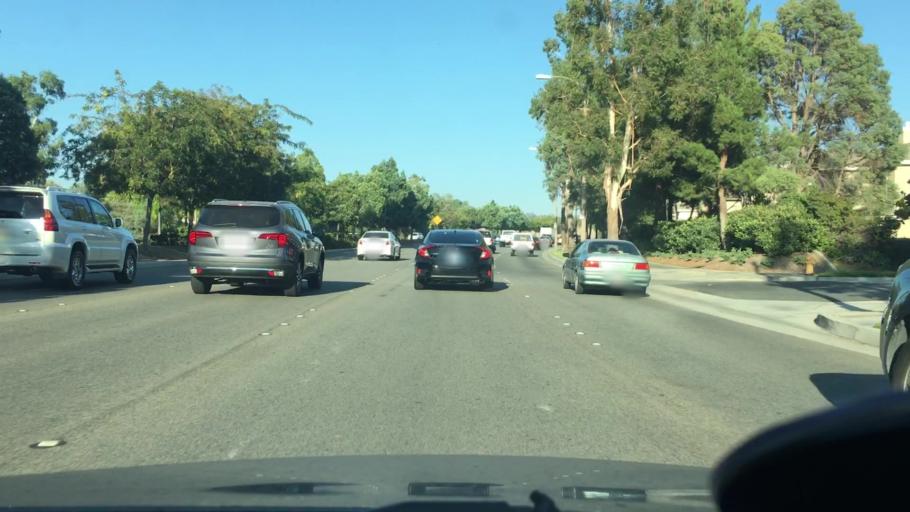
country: US
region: California
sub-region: Los Angeles County
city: Santa Clarita
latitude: 34.4283
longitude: -118.5430
